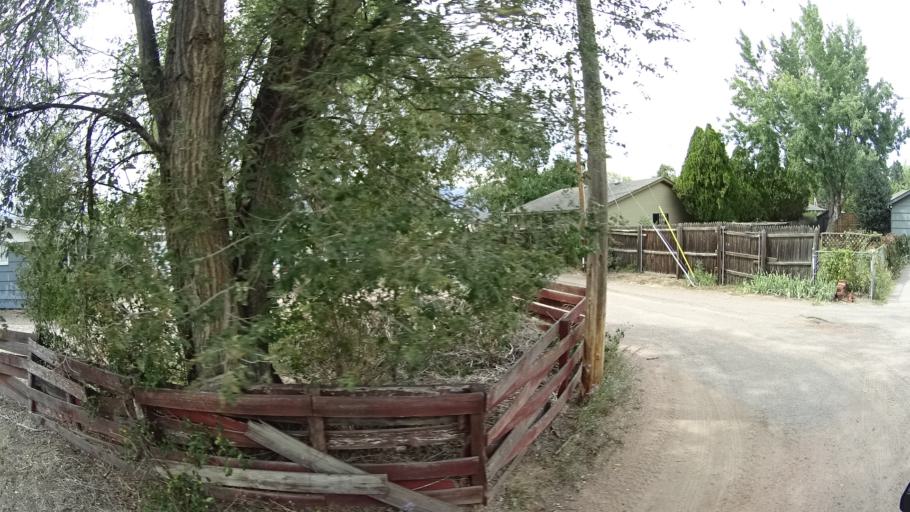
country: US
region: Colorado
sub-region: El Paso County
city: Colorado Springs
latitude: 38.8620
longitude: -104.7901
